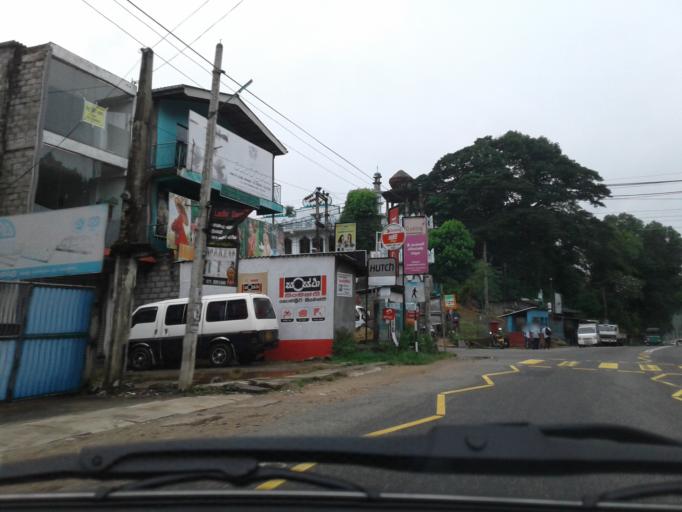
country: LK
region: North Western
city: Kurunegala
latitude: 7.2313
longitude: 80.2440
